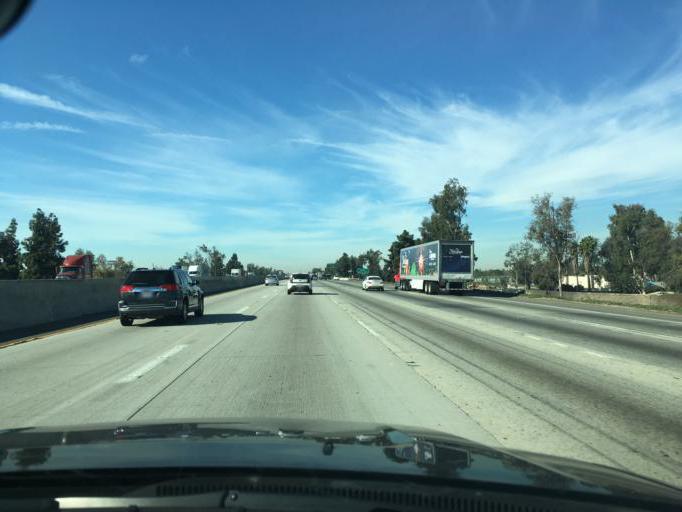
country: US
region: California
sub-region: San Bernardino County
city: Ontario
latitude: 34.0305
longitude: -117.6478
